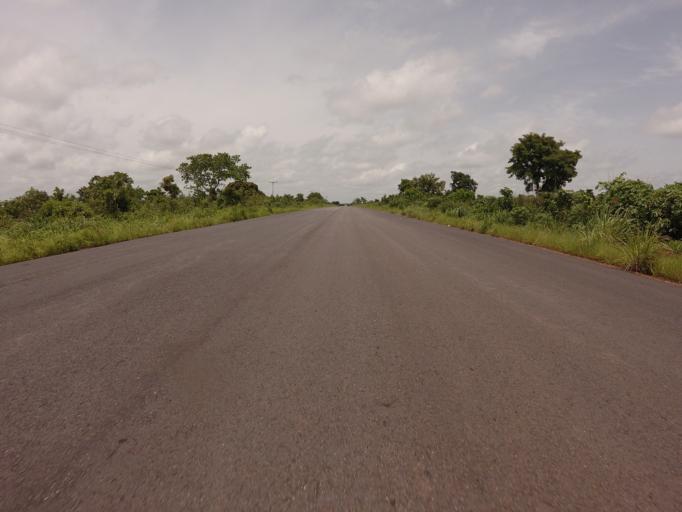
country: GH
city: Kpandae
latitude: 8.5605
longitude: 0.2554
